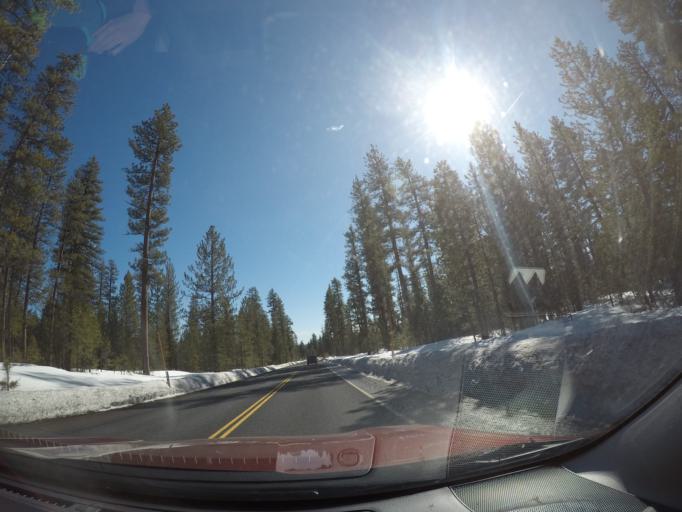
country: US
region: Oregon
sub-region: Deschutes County
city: Three Rivers
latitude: 43.8956
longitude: -121.5906
